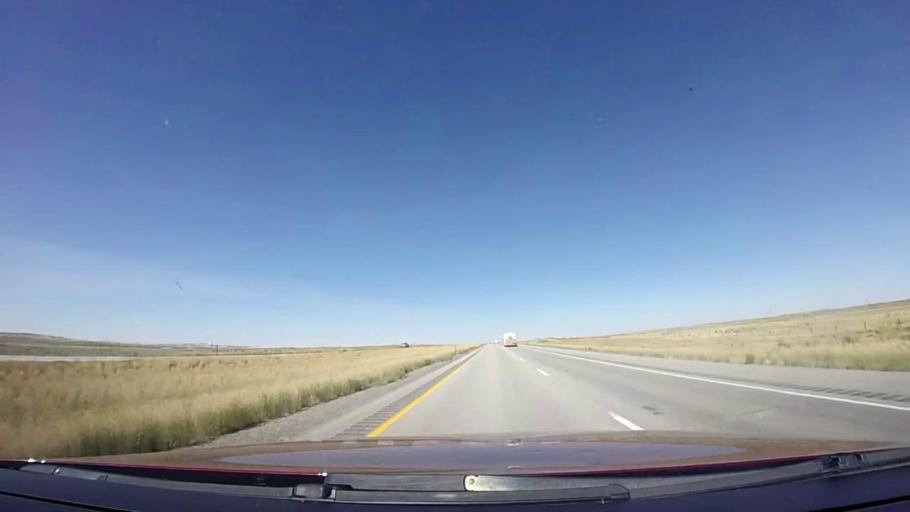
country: US
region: Wyoming
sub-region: Sweetwater County
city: Rock Springs
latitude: 41.6313
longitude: -108.3322
